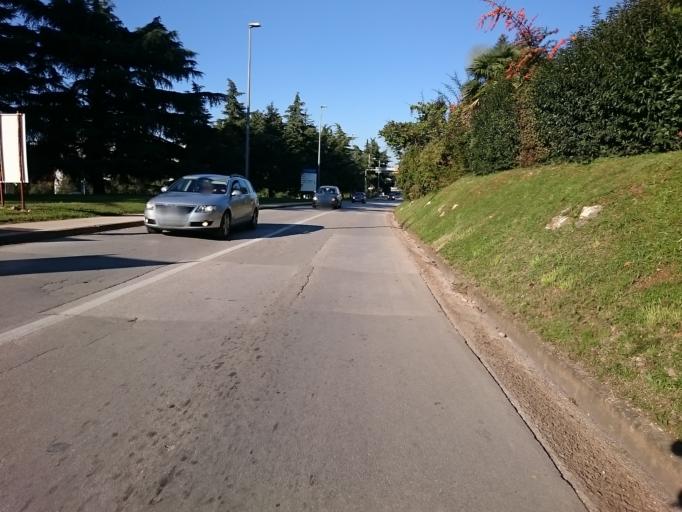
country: HR
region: Istarska
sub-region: Grad Porec
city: Porec
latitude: 45.2287
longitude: 13.6038
